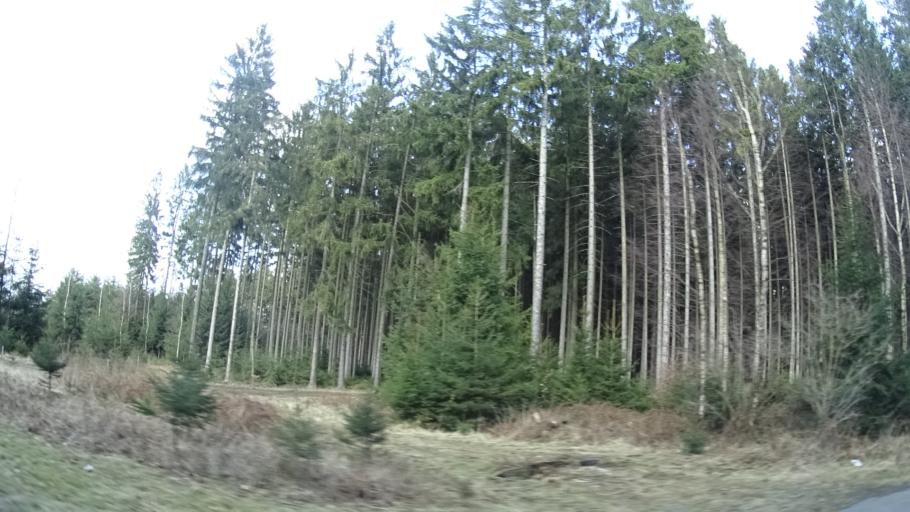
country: DE
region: Thuringia
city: Schleiz
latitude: 50.5522
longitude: 11.8361
